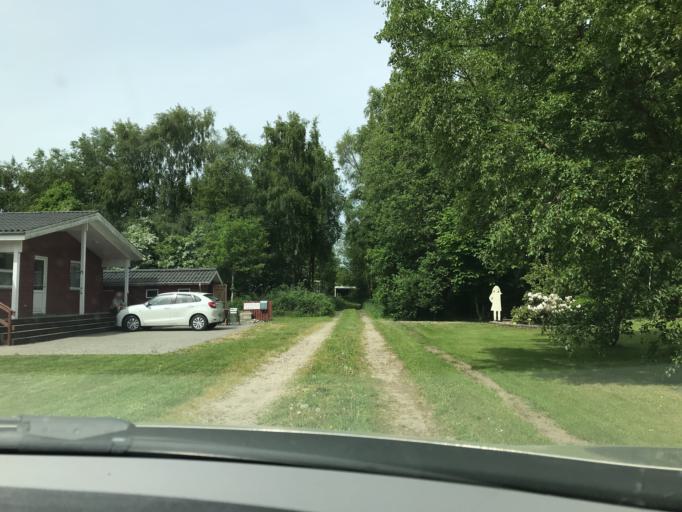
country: DK
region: Central Jutland
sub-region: Norddjurs Kommune
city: Allingabro
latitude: 56.5945
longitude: 10.3129
